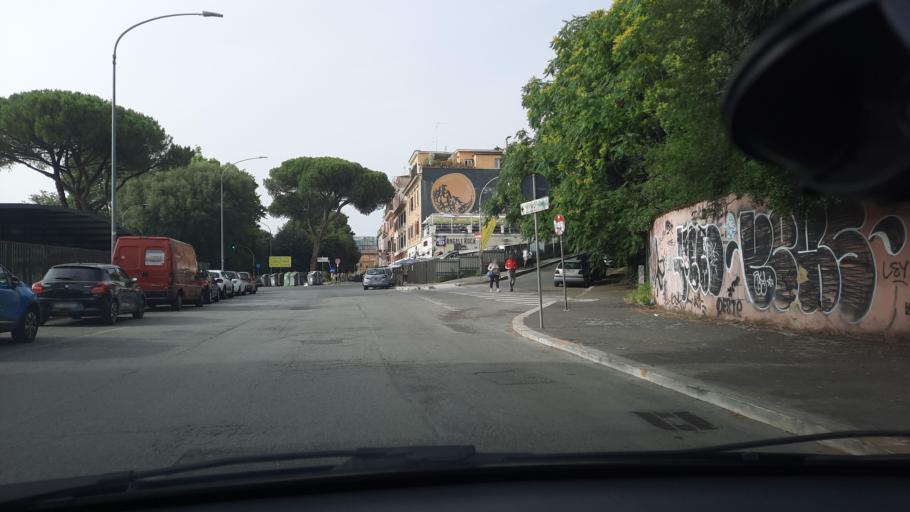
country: IT
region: Latium
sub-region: Citta metropolitana di Roma Capitale
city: Rome
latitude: 41.8597
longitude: 12.4783
